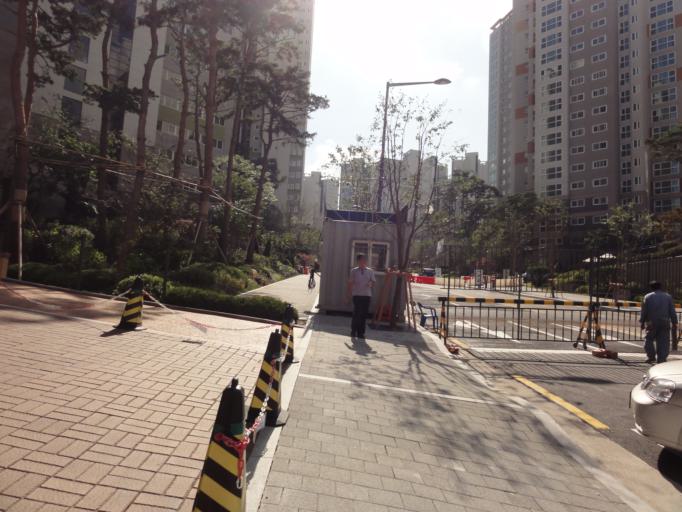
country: KR
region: Seoul
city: Seoul
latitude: 37.5552
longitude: 126.9550
